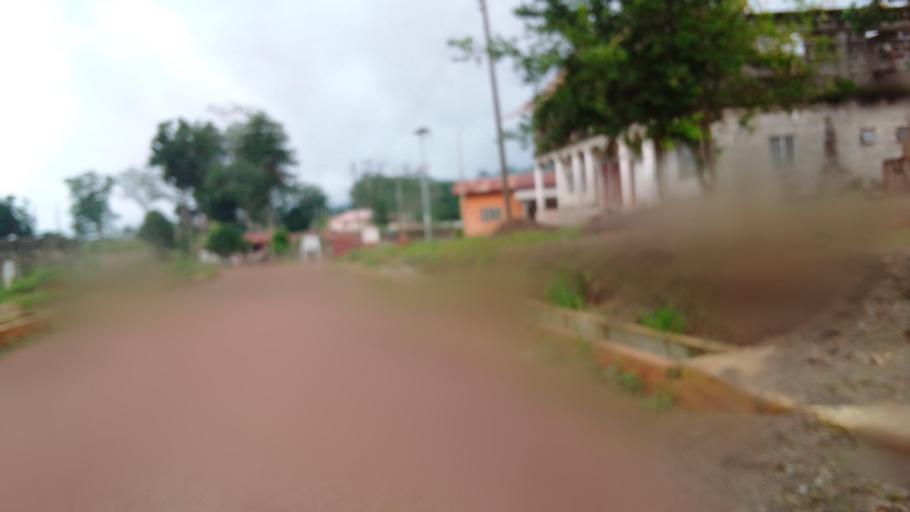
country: SL
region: Eastern Province
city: Kenema
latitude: 7.8868
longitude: -11.1924
